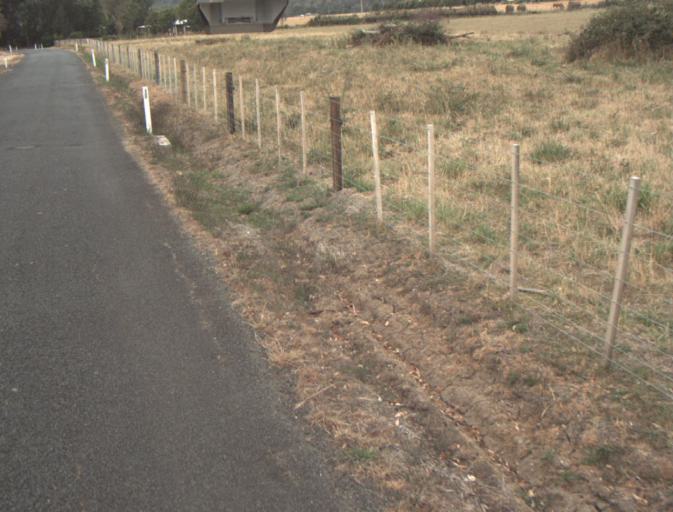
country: AU
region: Tasmania
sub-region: Launceston
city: Mayfield
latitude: -41.2872
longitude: 146.9968
